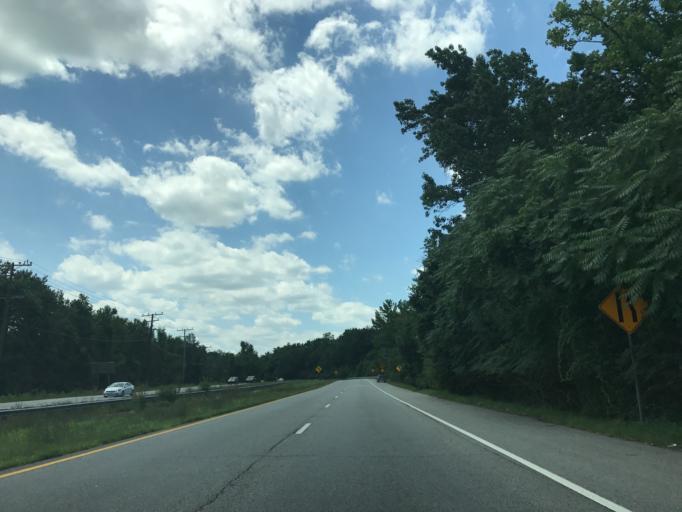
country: US
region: Maryland
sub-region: Anne Arundel County
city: Crofton
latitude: 38.9863
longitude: -76.7106
